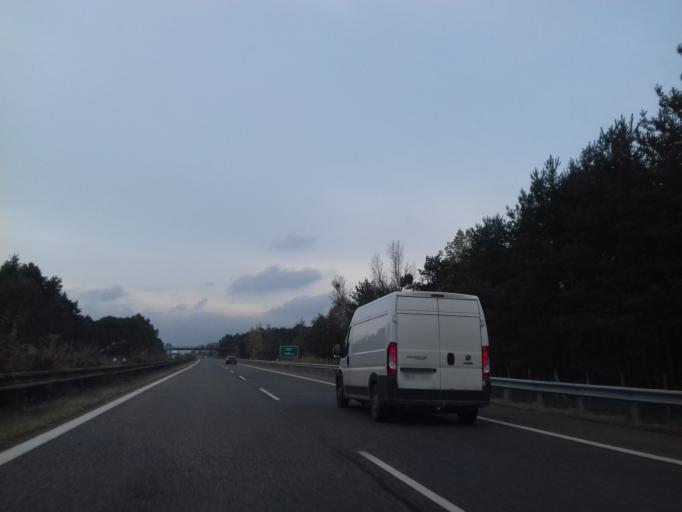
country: CZ
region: South Moravian
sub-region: Okres Breclav
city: Lanzhot
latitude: 48.6258
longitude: 17.0089
